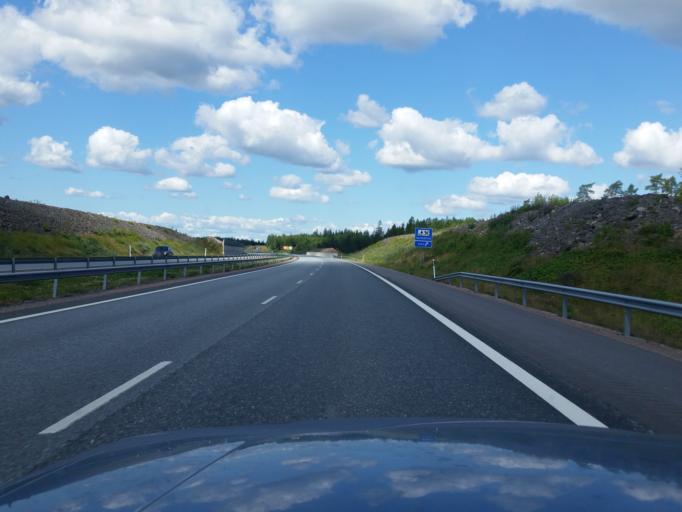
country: FI
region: Uusimaa
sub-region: Helsinki
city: Sammatti
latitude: 60.3640
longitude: 23.8801
